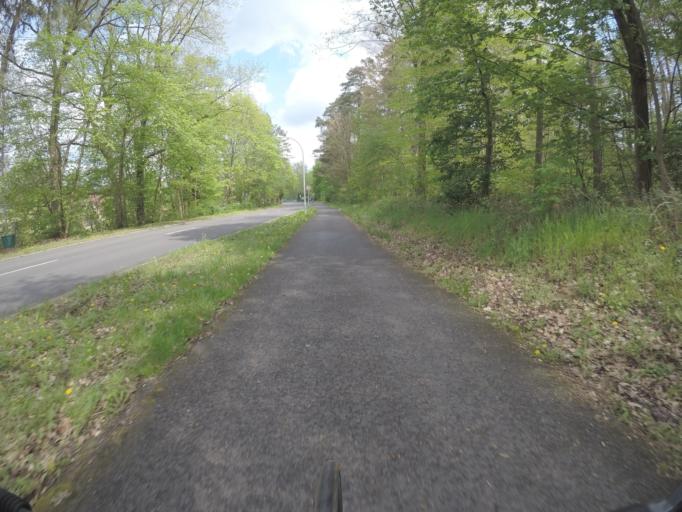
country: DE
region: Brandenburg
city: Marienwerder
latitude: 52.8891
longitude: 13.6385
